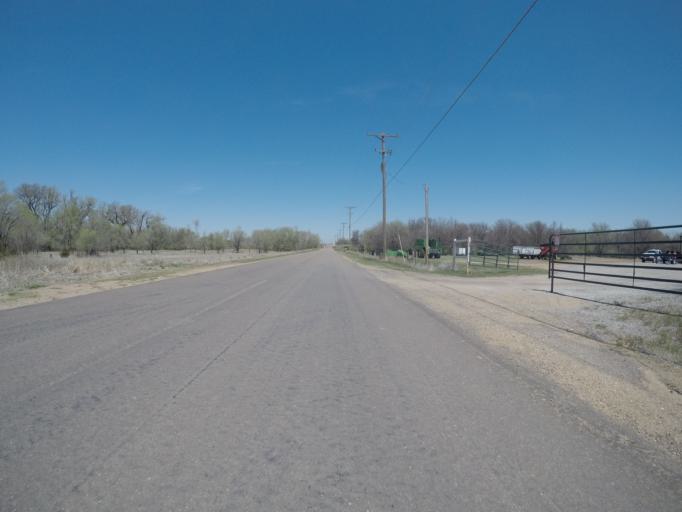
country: US
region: Kansas
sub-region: Pratt County
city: Pratt
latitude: 37.6380
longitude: -98.7669
